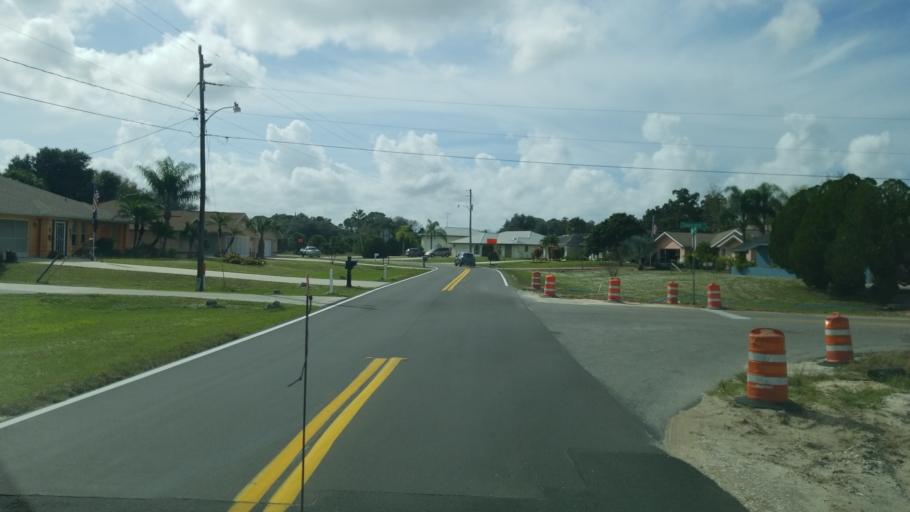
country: US
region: Florida
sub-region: Sarasota County
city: North Port
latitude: 27.0315
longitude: -82.2046
